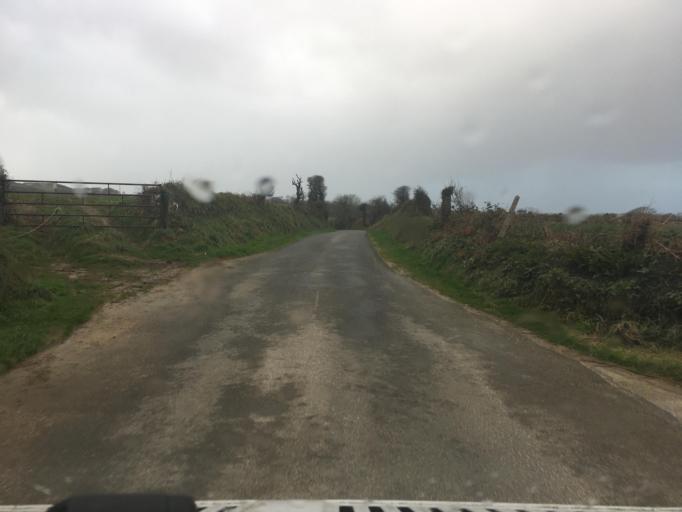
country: FR
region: Lower Normandy
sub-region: Departement de la Manche
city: Beaumont-Hague
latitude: 49.6872
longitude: -1.8811
